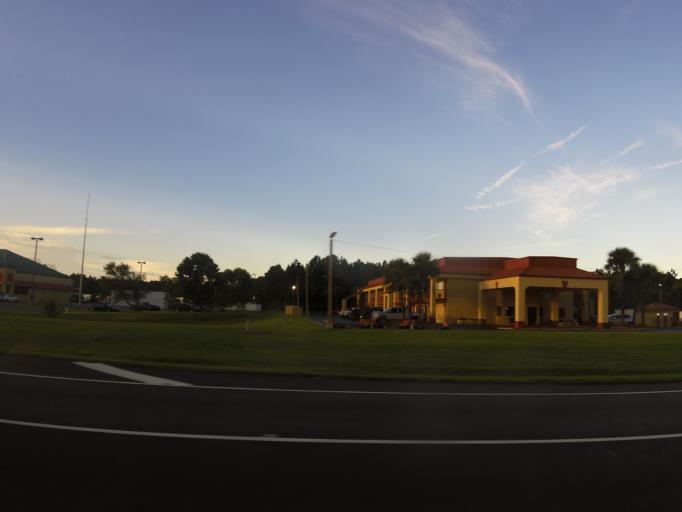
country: US
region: Georgia
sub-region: Camden County
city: Kingsland
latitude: 30.7929
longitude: -81.6658
